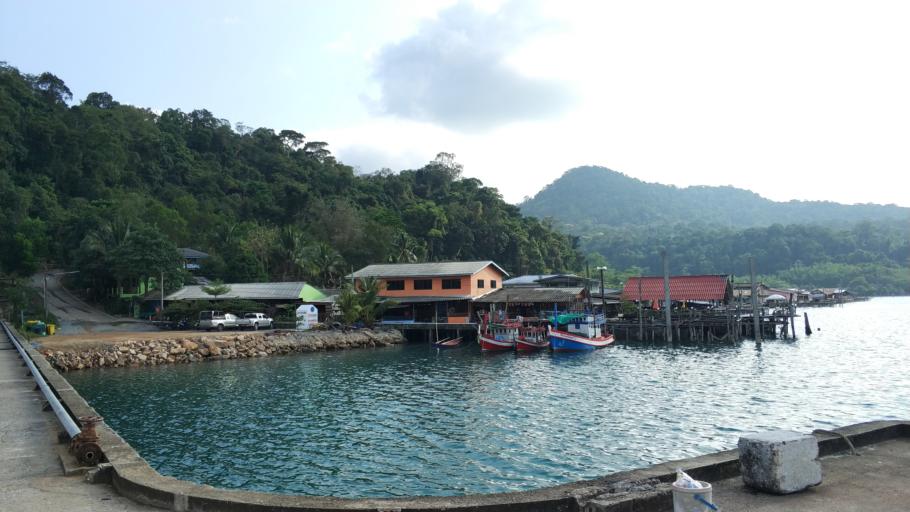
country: TH
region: Trat
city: Ko Kut
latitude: 11.6091
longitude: 102.5945
